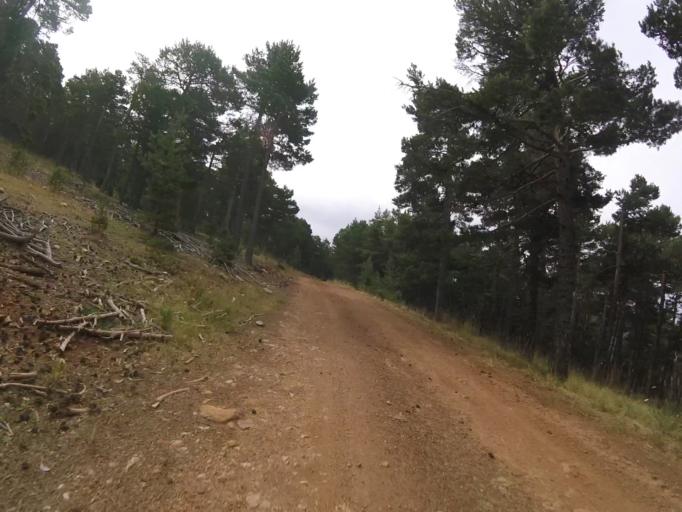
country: ES
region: Aragon
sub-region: Provincia de Teruel
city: Valdelinares
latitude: 40.3537
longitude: -0.5983
